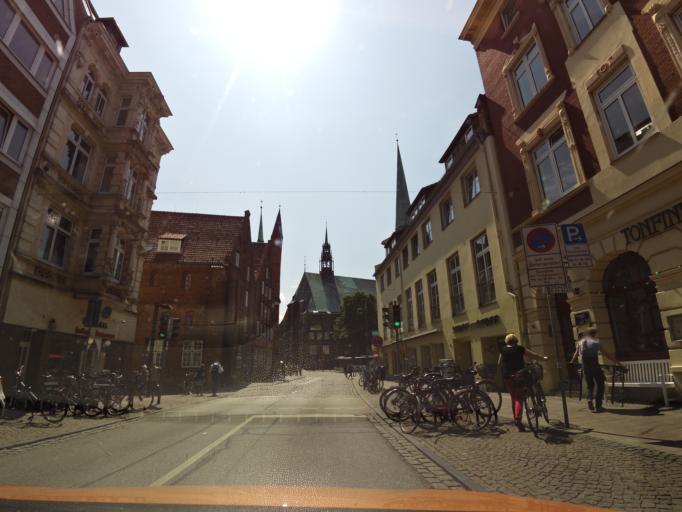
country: DE
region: Schleswig-Holstein
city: Luebeck
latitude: 53.8718
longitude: 10.6903
